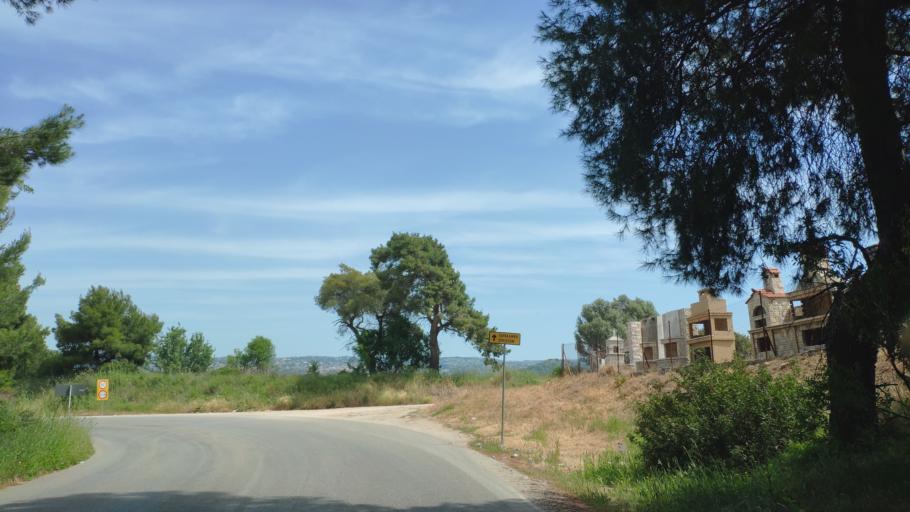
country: GR
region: Attica
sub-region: Nomarchia Anatolikis Attikis
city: Agios Stefanos
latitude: 38.1643
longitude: 23.8616
